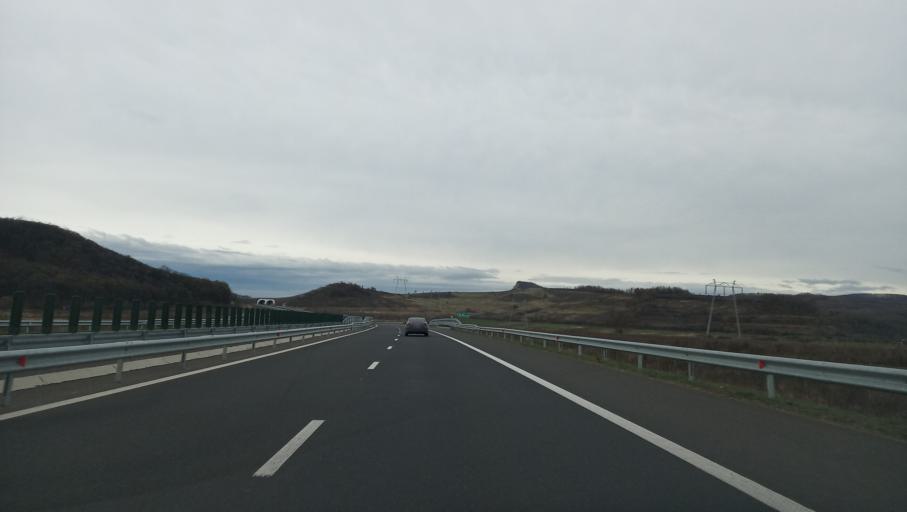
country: RO
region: Hunedoara
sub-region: Comuna Branisca
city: Branisca
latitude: 45.9351
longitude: 22.7558
